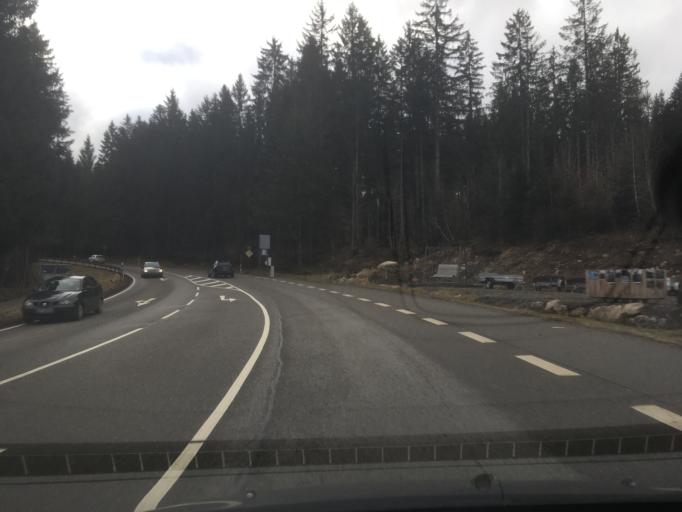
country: DE
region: Baden-Wuerttemberg
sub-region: Freiburg Region
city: Hausern
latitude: 47.7462
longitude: 8.1664
